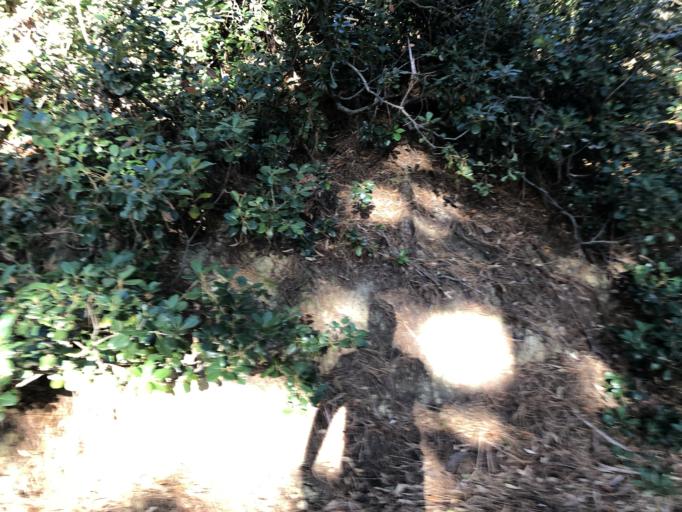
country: NZ
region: Wellington
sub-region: Wellington City
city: Wellington
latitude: -41.2996
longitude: 174.7886
